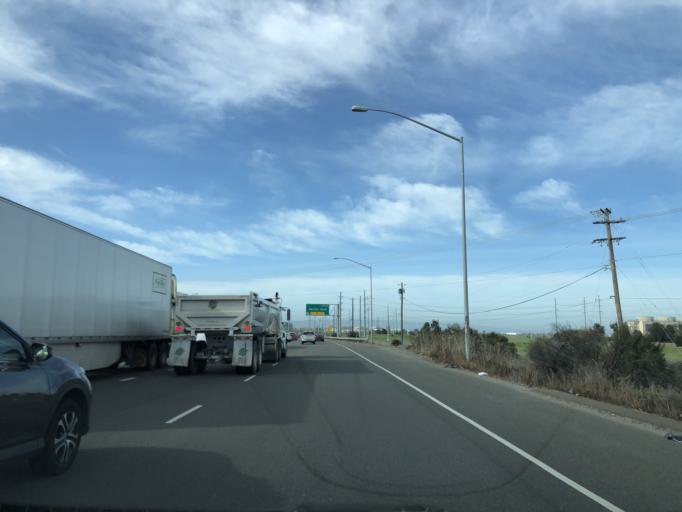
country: US
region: California
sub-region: Santa Clara County
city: Milpitas
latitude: 37.4231
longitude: -121.9297
